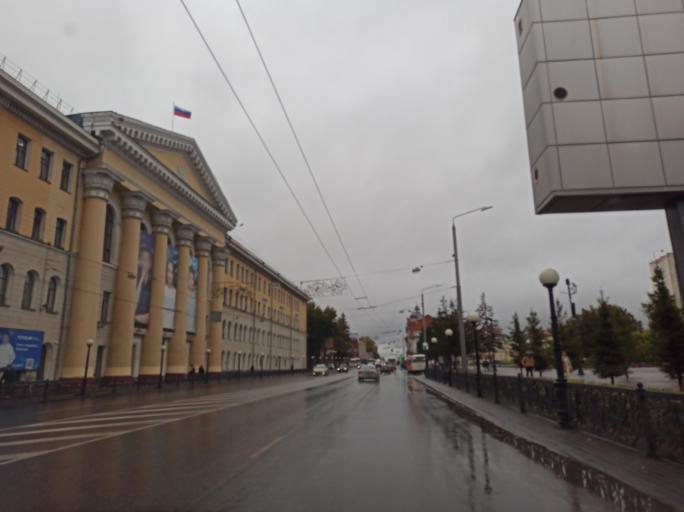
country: RU
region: Tomsk
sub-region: Tomskiy Rayon
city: Tomsk
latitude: 56.4736
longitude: 84.9504
